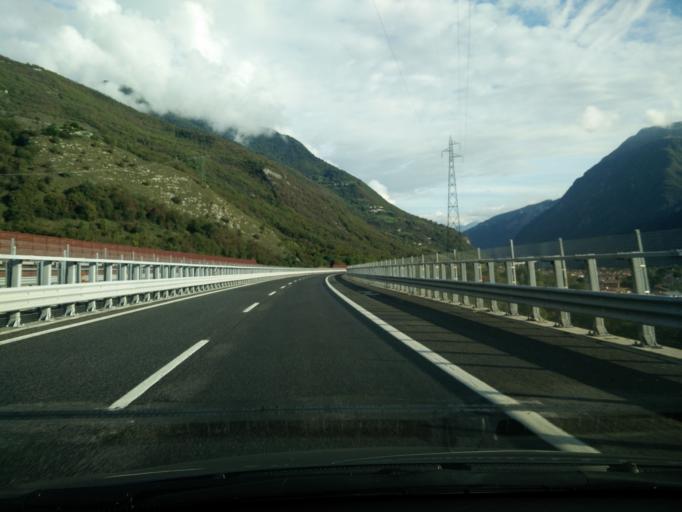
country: IT
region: Veneto
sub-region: Provincia di Treviso
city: Revine
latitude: 46.0079
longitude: 12.2763
